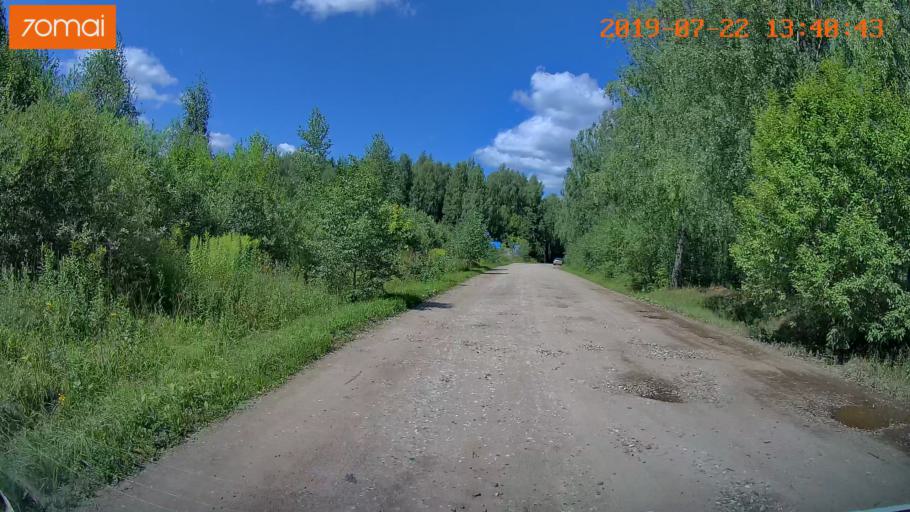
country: RU
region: Ivanovo
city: Novo-Talitsy
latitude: 57.0773
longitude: 40.8807
